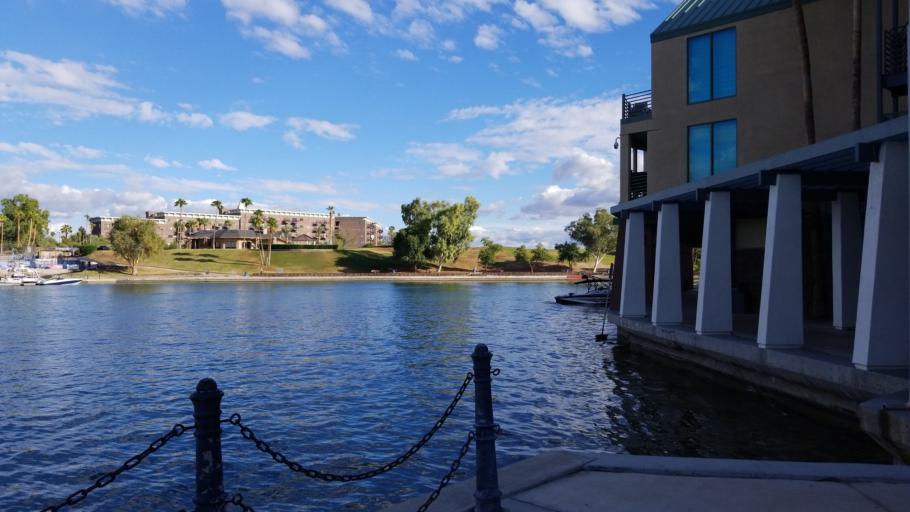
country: US
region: Arizona
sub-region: Mohave County
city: Lake Havasu City
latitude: 34.4708
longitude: -114.3478
